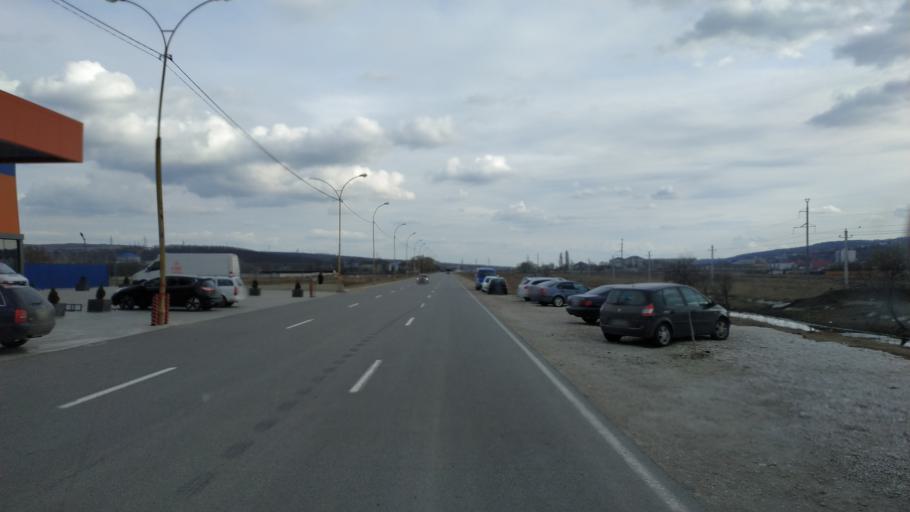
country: MD
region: Hincesti
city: Hincesti
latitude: 46.8299
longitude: 28.5999
